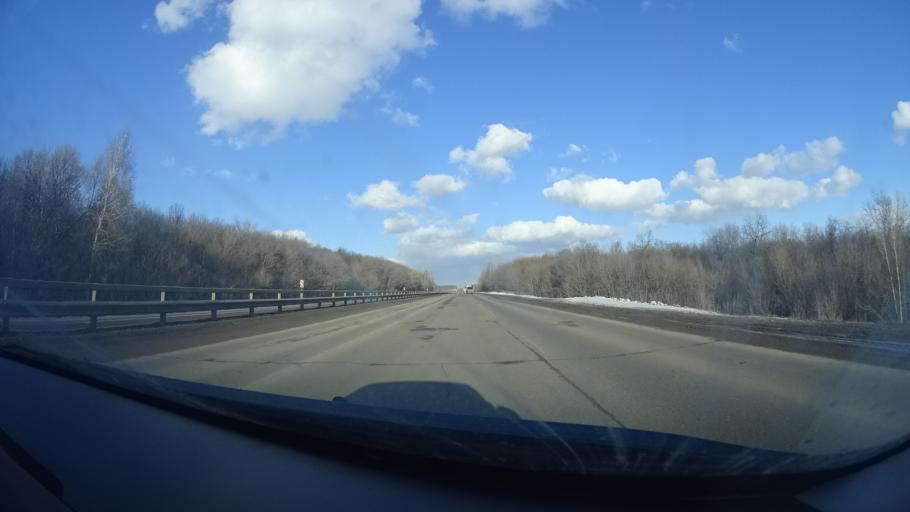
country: RU
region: Bashkortostan
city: Avdon
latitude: 54.6440
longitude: 55.6253
